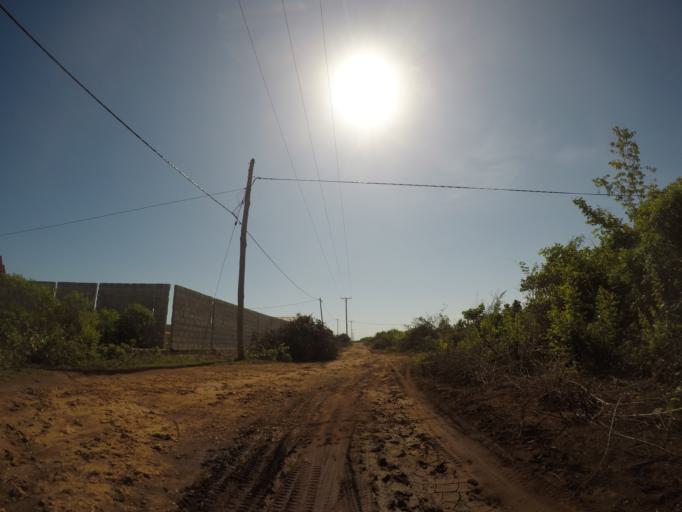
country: TZ
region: Zanzibar Central/South
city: Koani
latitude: -6.2091
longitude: 39.3026
